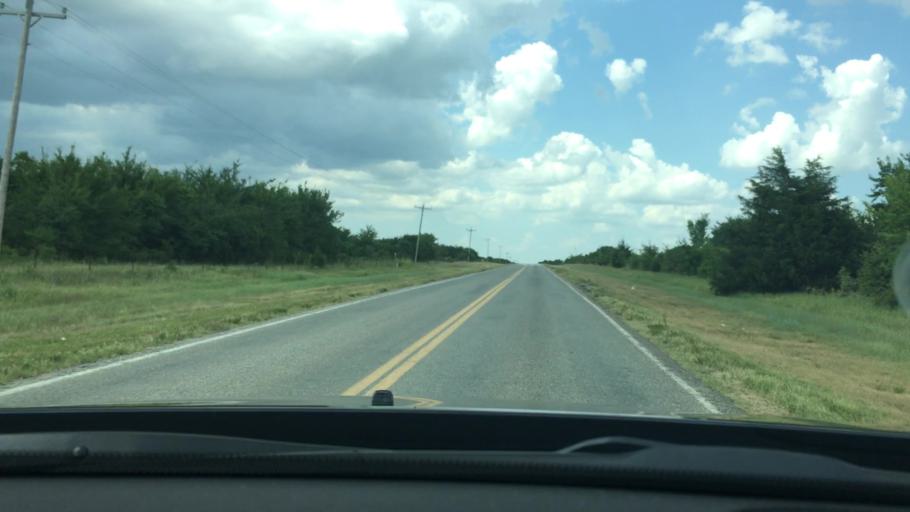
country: US
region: Oklahoma
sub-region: Pontotoc County
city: Ada
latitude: 34.5364
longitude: -96.6346
